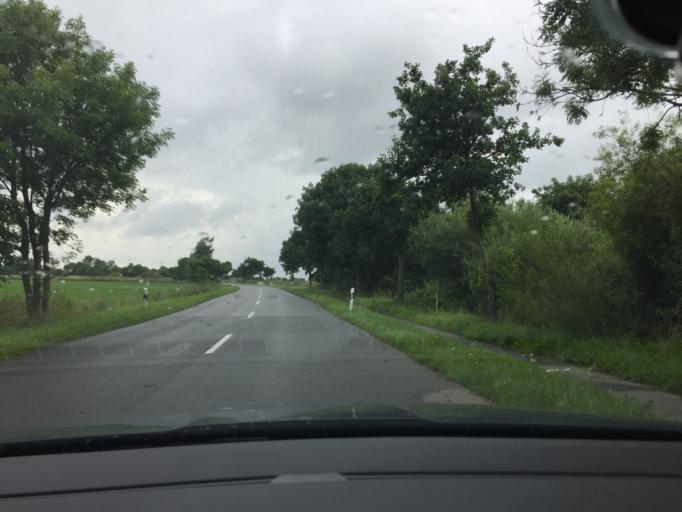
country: DE
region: Lower Saxony
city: Wirdum
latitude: 53.4941
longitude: 7.0675
